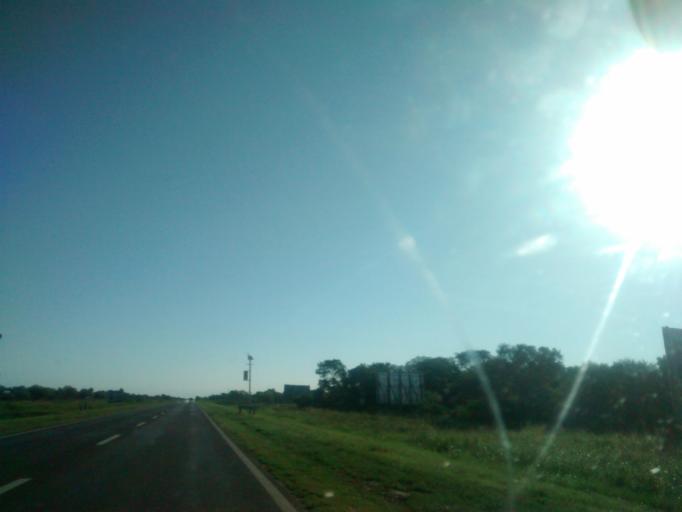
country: AR
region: Chaco
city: Fontana
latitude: -27.4792
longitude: -59.0606
